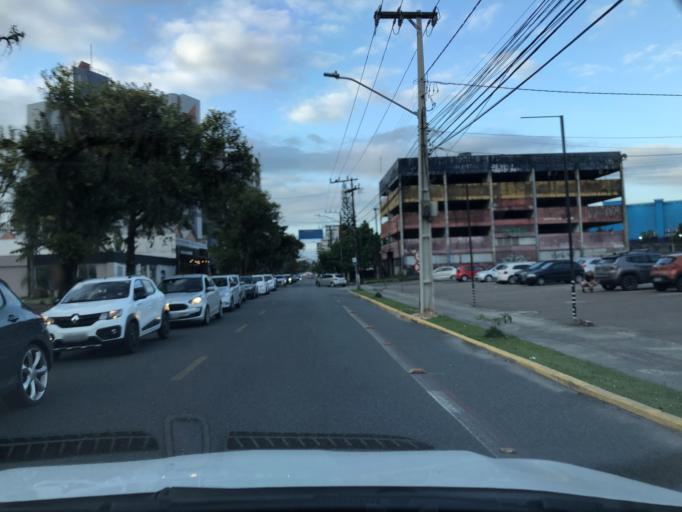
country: BR
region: Santa Catarina
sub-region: Joinville
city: Joinville
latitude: -26.2925
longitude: -48.8456
